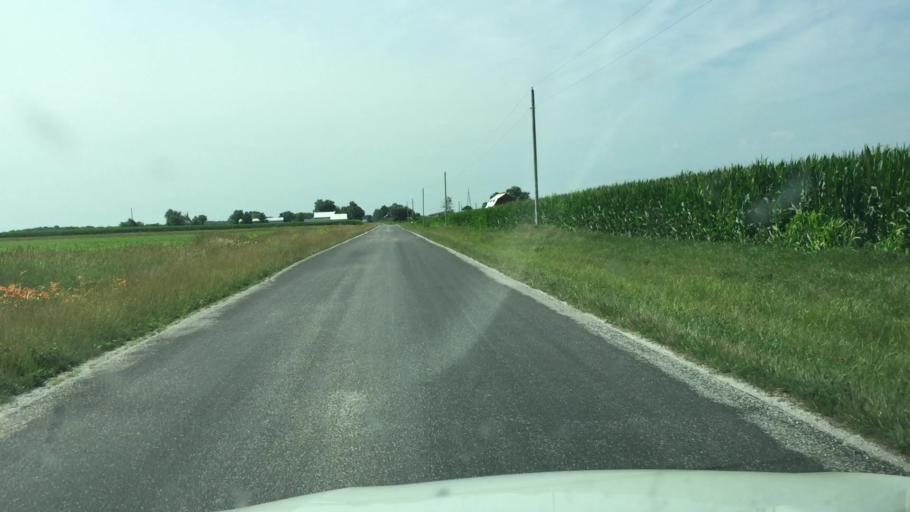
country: US
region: Illinois
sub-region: Hancock County
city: Nauvoo
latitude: 40.5102
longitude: -91.3278
